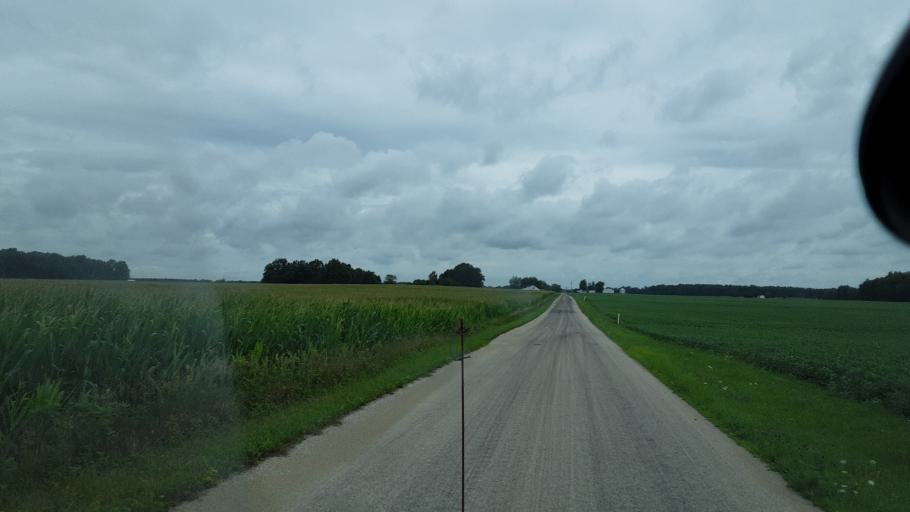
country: US
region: Indiana
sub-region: Jay County
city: Portland
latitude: 40.4996
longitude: -85.0093
